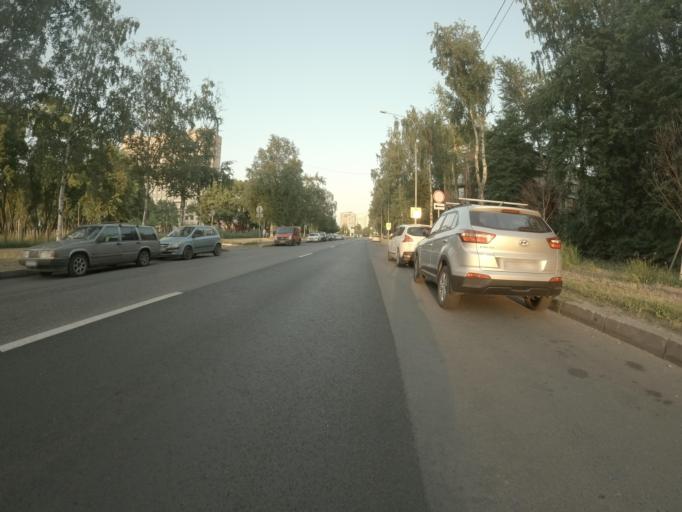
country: RU
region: Leningrad
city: Kalininskiy
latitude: 59.9784
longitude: 30.4276
